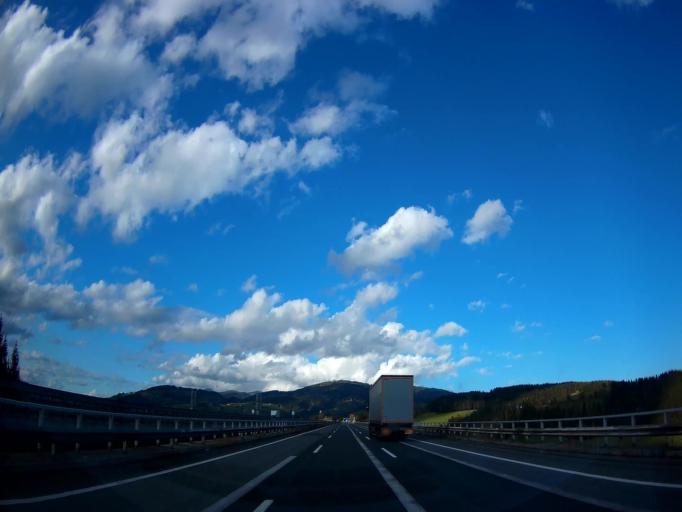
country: AT
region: Carinthia
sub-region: Politischer Bezirk Wolfsberg
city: Bad Sankt Leonhard im Lavanttal
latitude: 46.9180
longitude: 14.8391
